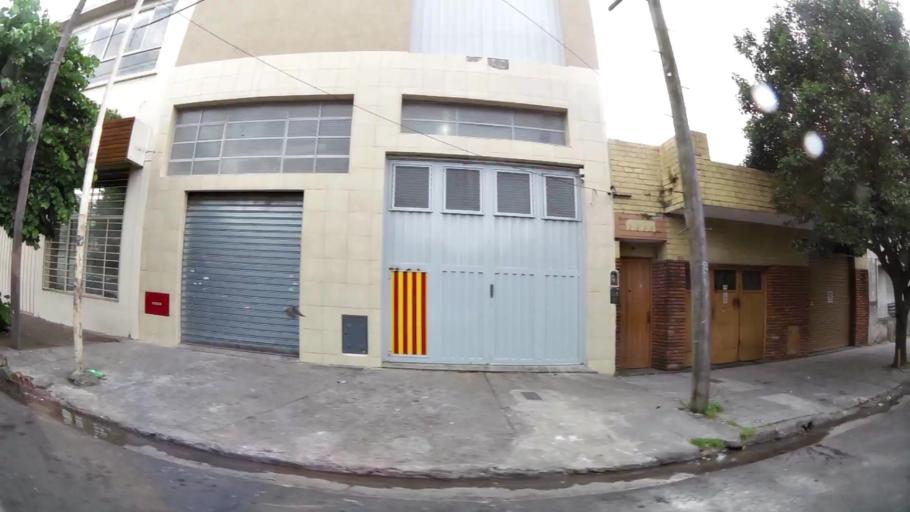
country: AR
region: Buenos Aires
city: San Justo
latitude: -34.6618
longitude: -58.5254
